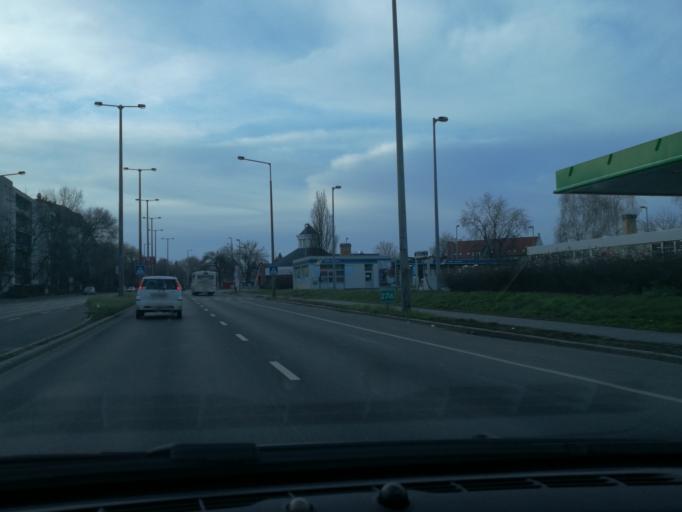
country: HU
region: Szabolcs-Szatmar-Bereg
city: Nyiregyhaza
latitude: 47.9462
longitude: 21.7259
